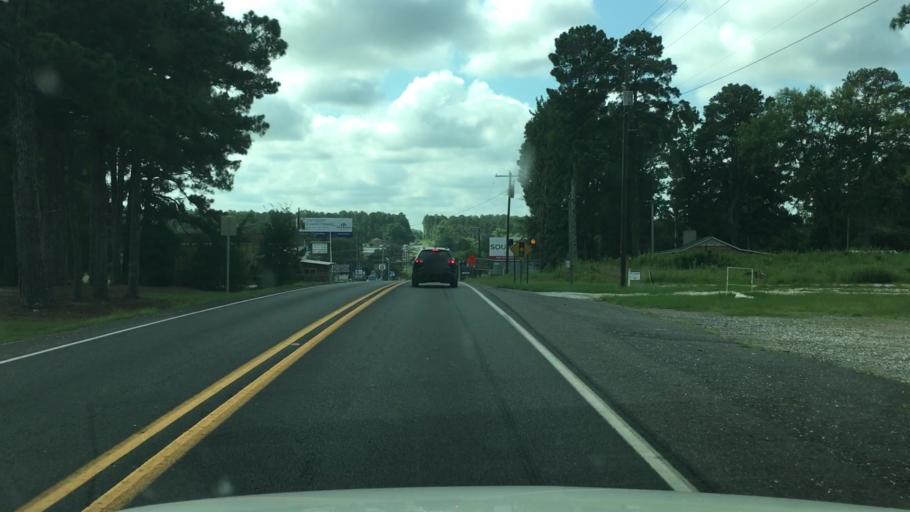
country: US
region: Arkansas
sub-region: Garland County
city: Lake Hamilton
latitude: 34.3186
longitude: -93.1718
